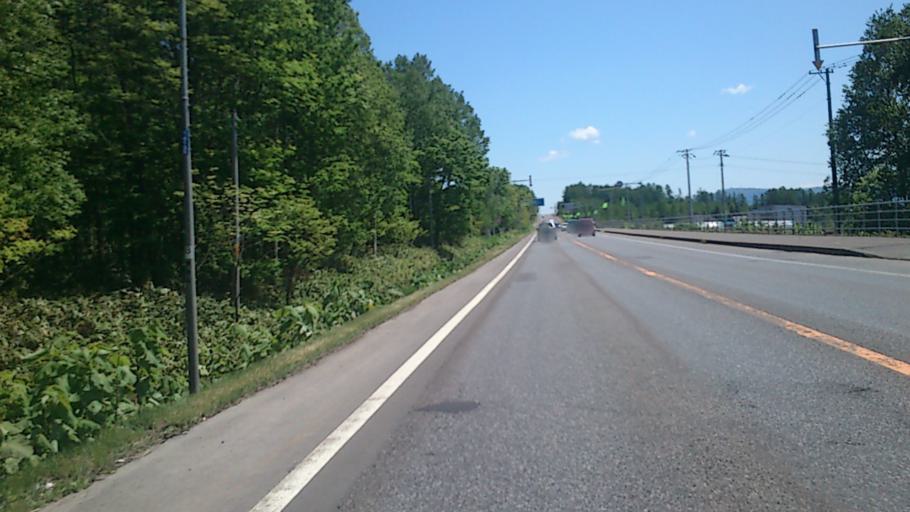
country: JP
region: Hokkaido
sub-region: Asahikawa-shi
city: Asahikawa
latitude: 44.0606
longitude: 142.4030
